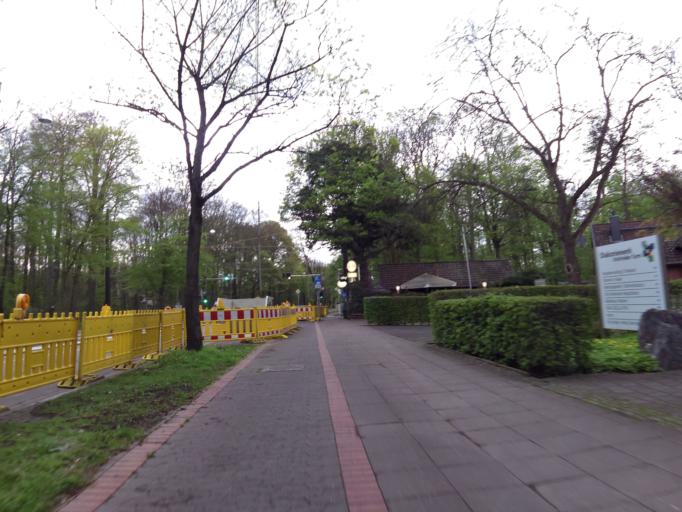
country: DE
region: Lower Saxony
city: Laatzen
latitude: 52.3667
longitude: 9.8121
